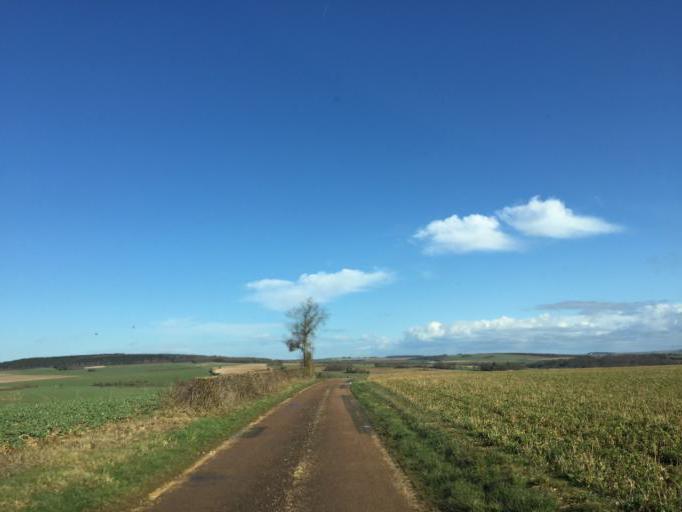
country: FR
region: Bourgogne
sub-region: Departement de l'Yonne
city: Fontenailles
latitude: 47.5493
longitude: 3.3305
